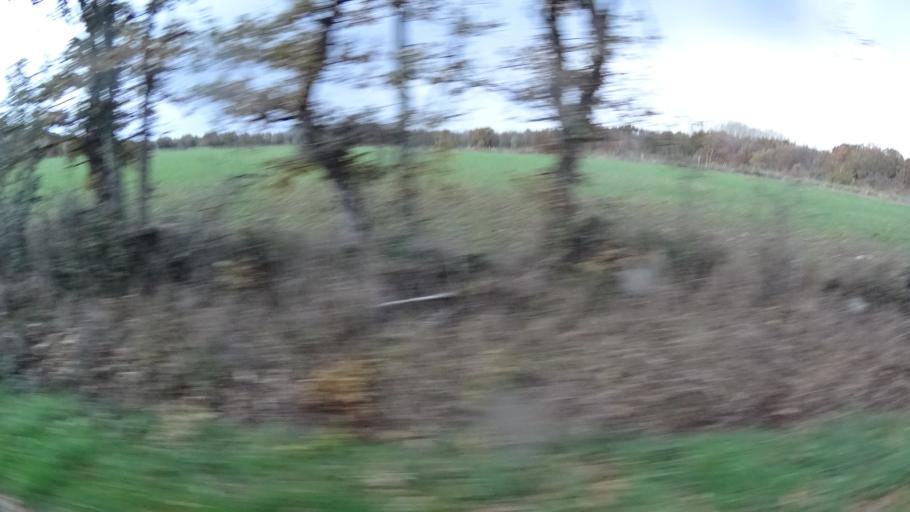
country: FR
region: Pays de la Loire
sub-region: Departement de la Loire-Atlantique
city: Avessac
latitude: 47.6633
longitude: -2.0252
